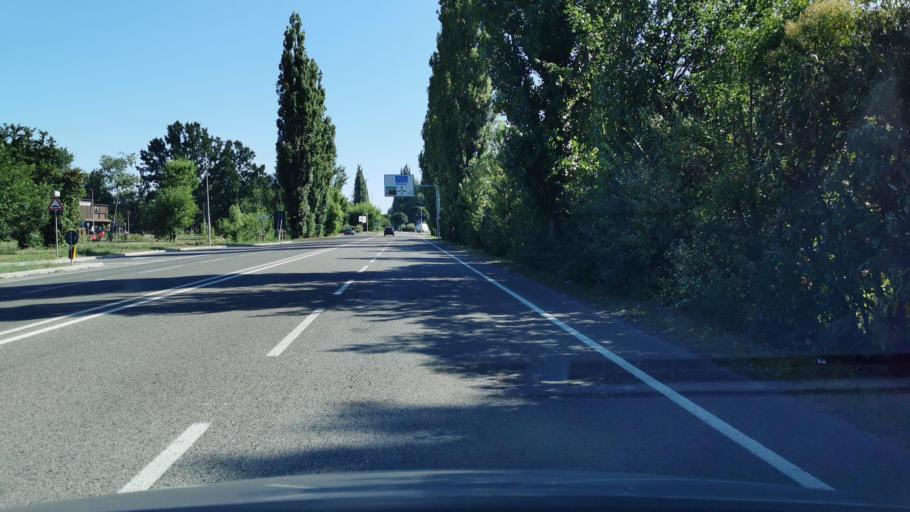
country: IT
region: Emilia-Romagna
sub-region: Provincia di Modena
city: Carpi Centro
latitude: 44.7792
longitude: 10.8660
